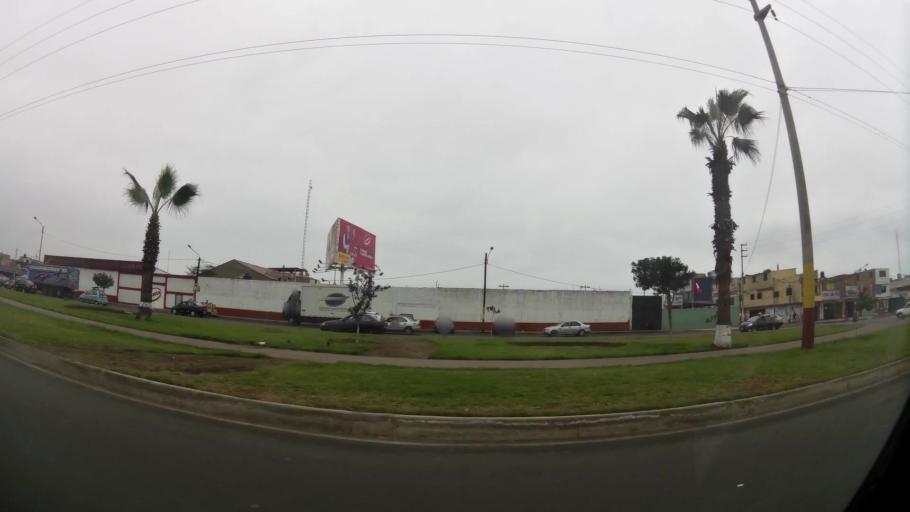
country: PE
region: Ancash
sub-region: Provincia de Santa
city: Chimbote
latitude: -9.0778
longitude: -78.5845
